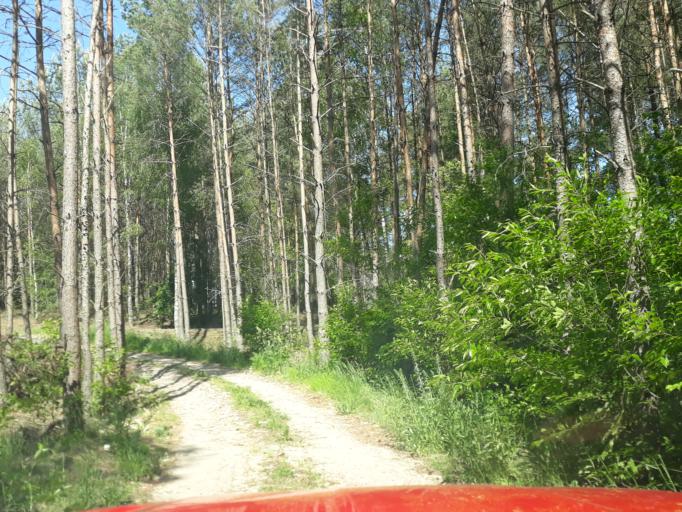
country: PL
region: Pomeranian Voivodeship
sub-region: Powiat chojnicki
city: Chojnice
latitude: 53.8728
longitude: 17.5397
